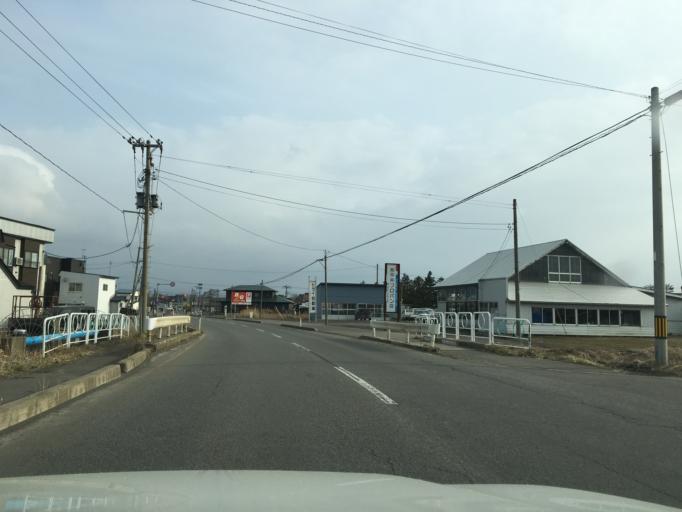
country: JP
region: Aomori
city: Namioka
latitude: 40.7192
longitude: 140.5889
